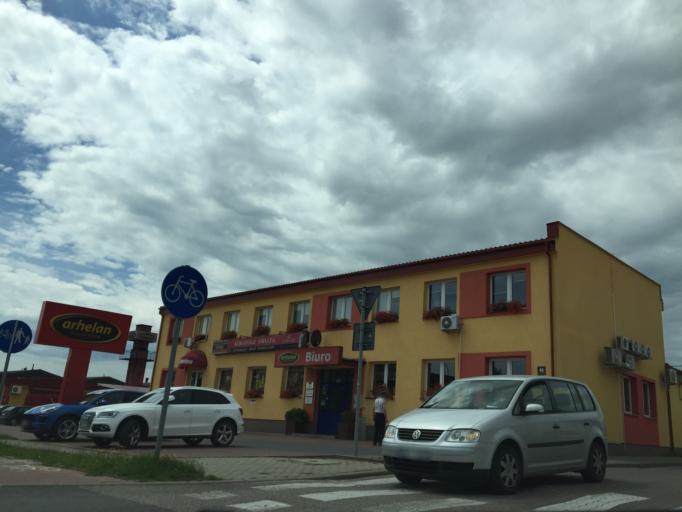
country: PL
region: Podlasie
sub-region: Powiat bielski
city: Bielsk Podlaski
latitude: 52.7756
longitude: 23.1858
